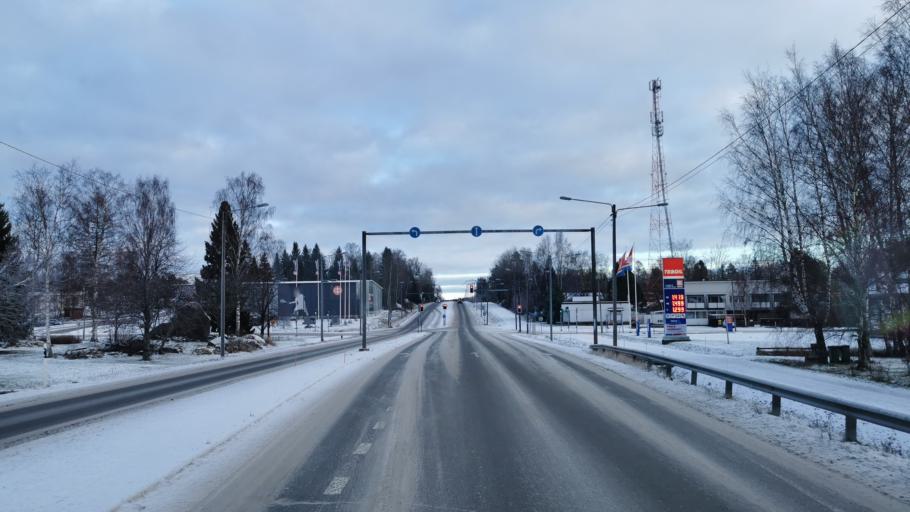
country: FI
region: Ostrobothnia
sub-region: Vaasa
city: Korsholm
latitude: 63.1145
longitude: 21.6838
